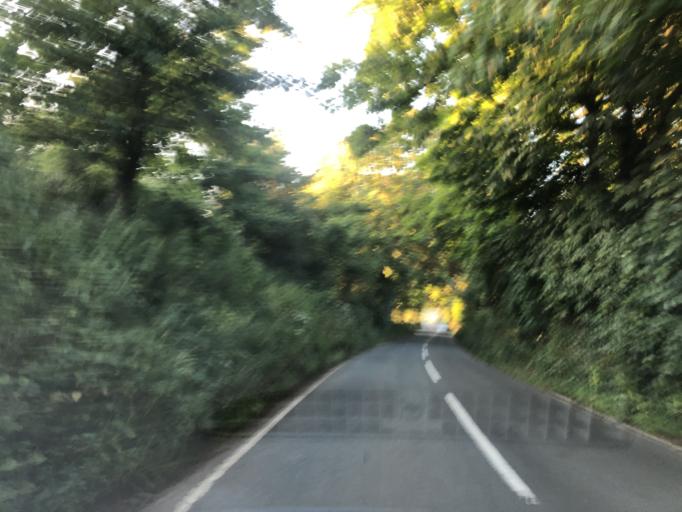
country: GB
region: England
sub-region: Isle of Wight
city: Niton
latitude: 50.6058
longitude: -1.2793
